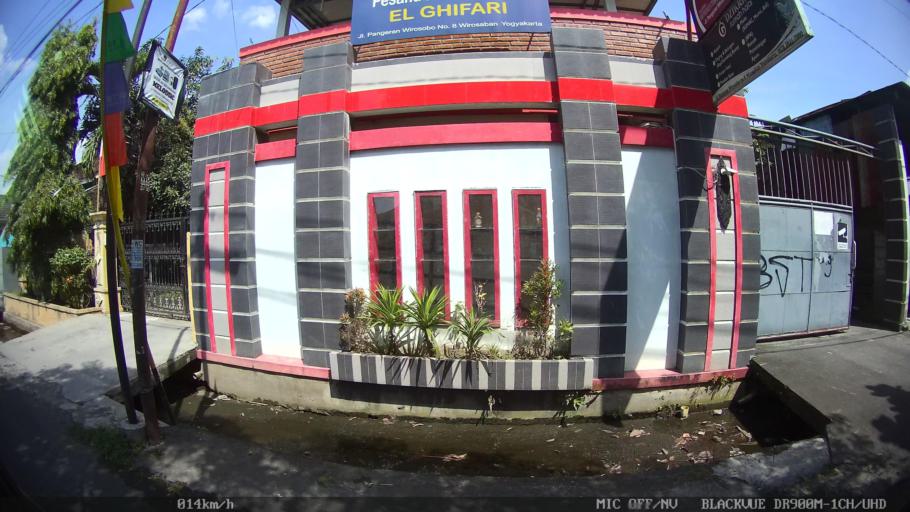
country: ID
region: Daerah Istimewa Yogyakarta
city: Yogyakarta
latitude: -7.8264
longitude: 110.3773
